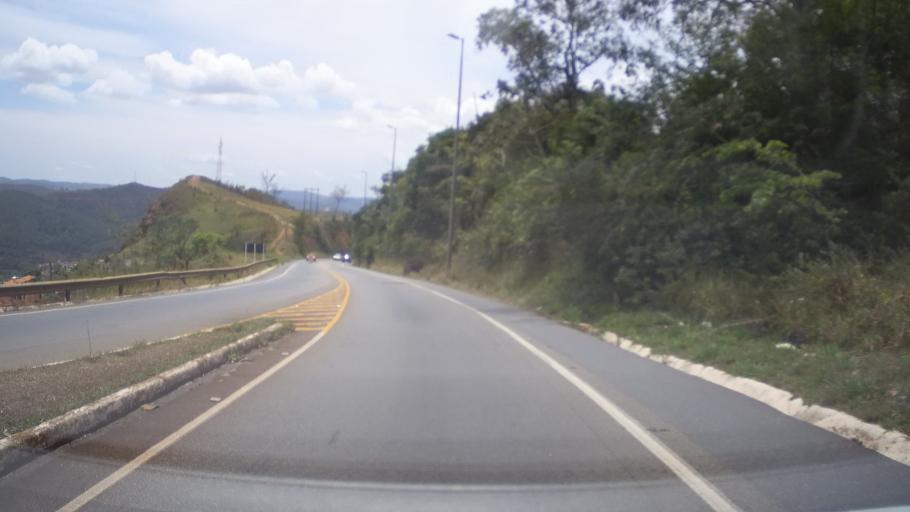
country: BR
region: Minas Gerais
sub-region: Nova Lima
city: Nova Lima
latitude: -19.9898
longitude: -43.8623
